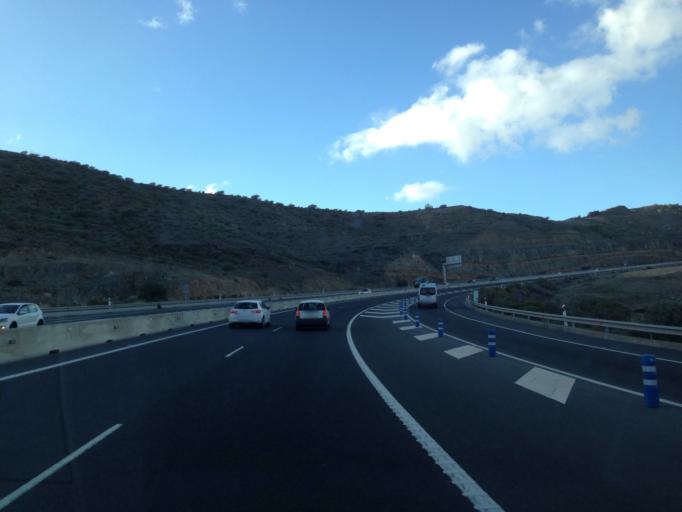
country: ES
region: Canary Islands
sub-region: Provincia de Las Palmas
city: Puerto Rico
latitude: 27.7660
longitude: -15.6732
